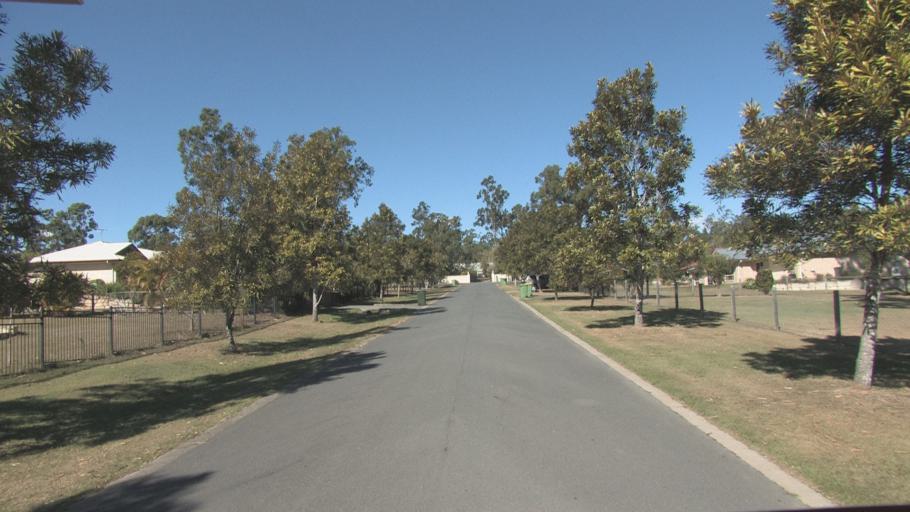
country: AU
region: Queensland
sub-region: Logan
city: North Maclean
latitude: -27.7570
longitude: 152.9537
